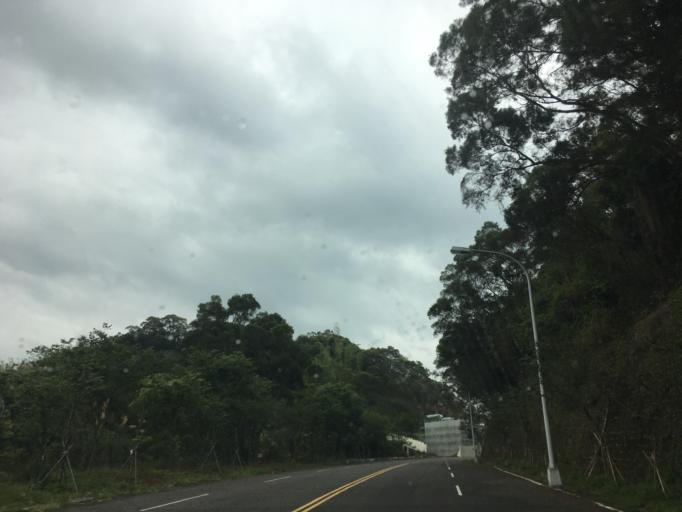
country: TW
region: Taiwan
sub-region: Taichung City
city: Taichung
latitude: 24.0634
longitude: 120.7242
